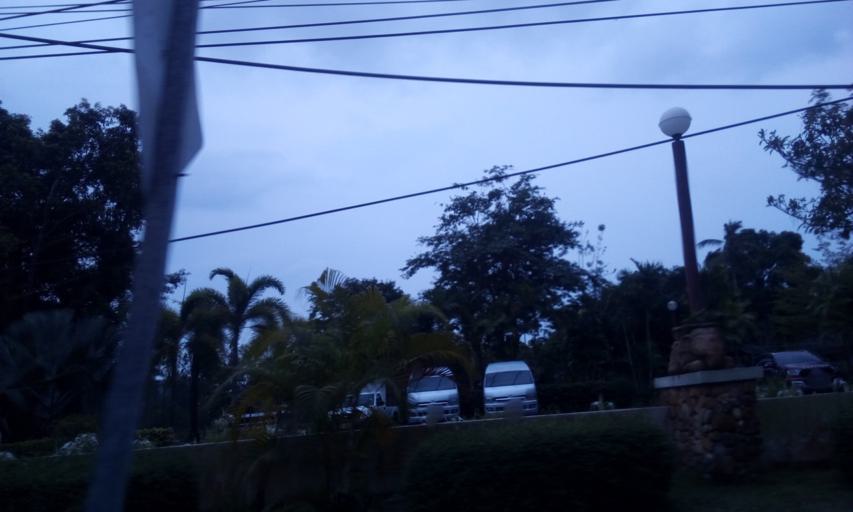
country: TH
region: Trat
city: Ko Chang Tai
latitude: 12.0582
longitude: 102.2964
